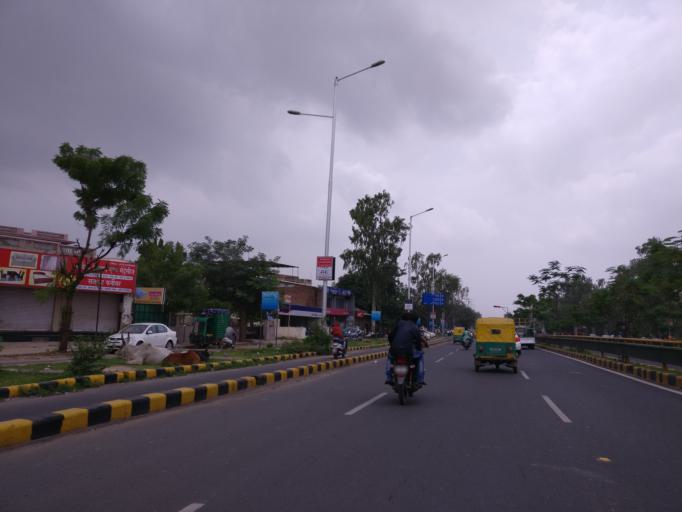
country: IN
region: Gujarat
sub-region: Gandhinagar
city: Adalaj
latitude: 23.1105
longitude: 72.5846
